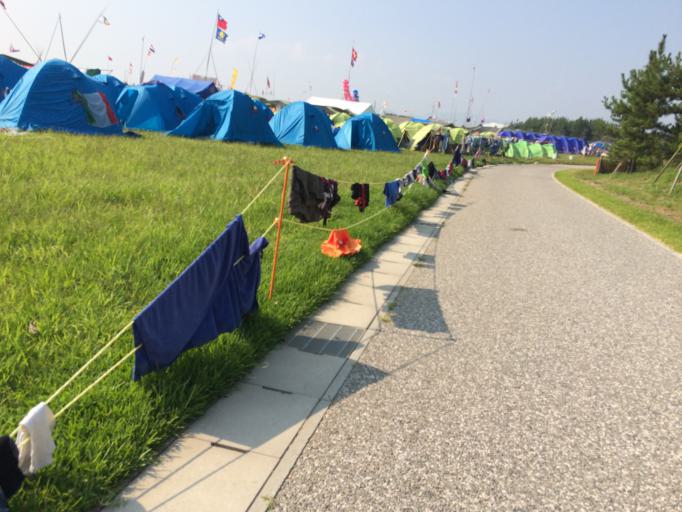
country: JP
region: Yamaguchi
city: Ogori-shimogo
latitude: 34.0107
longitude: 131.3780
